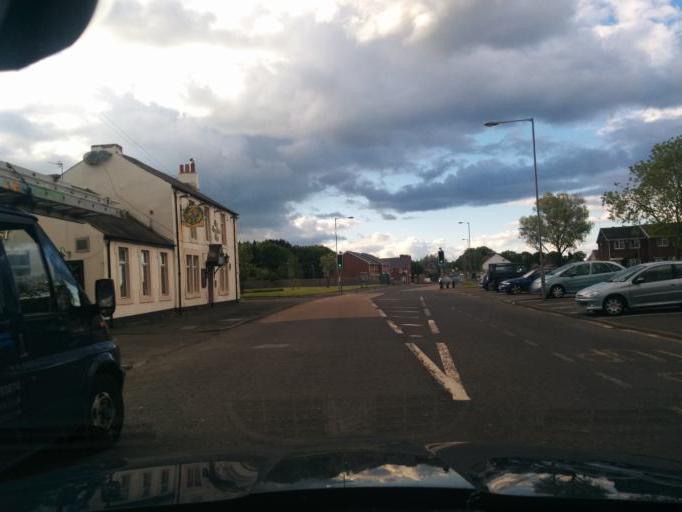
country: GB
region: England
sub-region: Northumberland
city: Choppington
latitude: 55.1501
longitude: -1.6026
